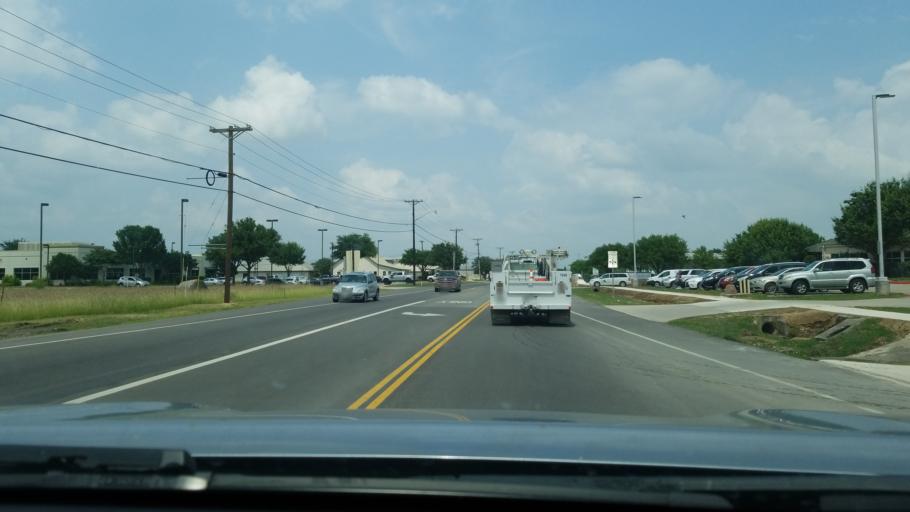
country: US
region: Texas
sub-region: Comal County
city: New Braunfels
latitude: 29.7224
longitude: -98.1005
